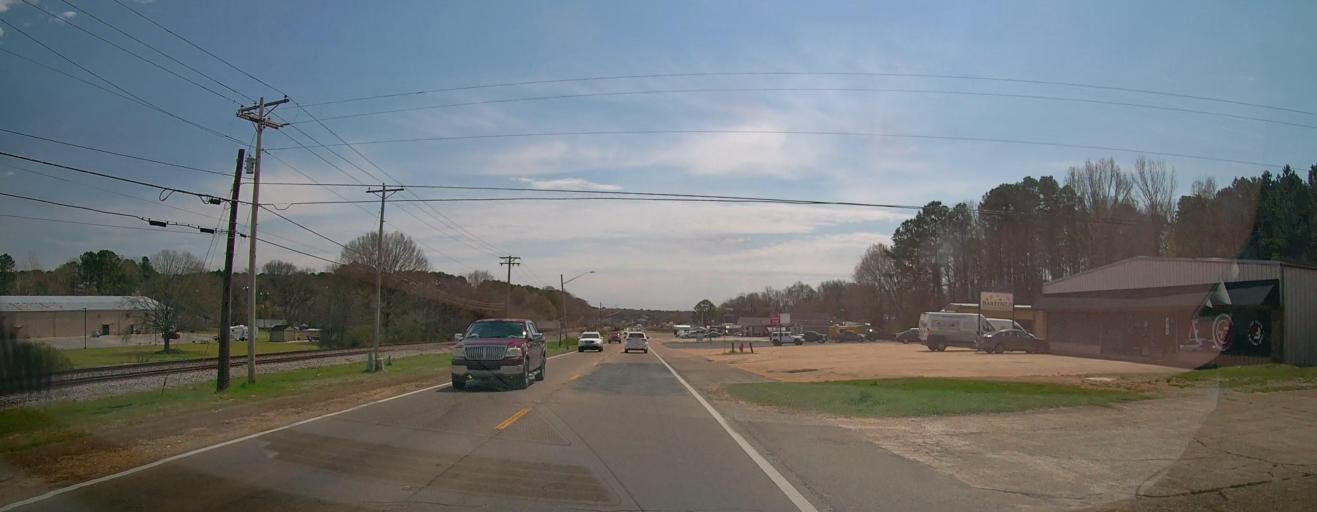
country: US
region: Mississippi
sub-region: Union County
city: New Albany
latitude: 34.5033
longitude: -89.0279
